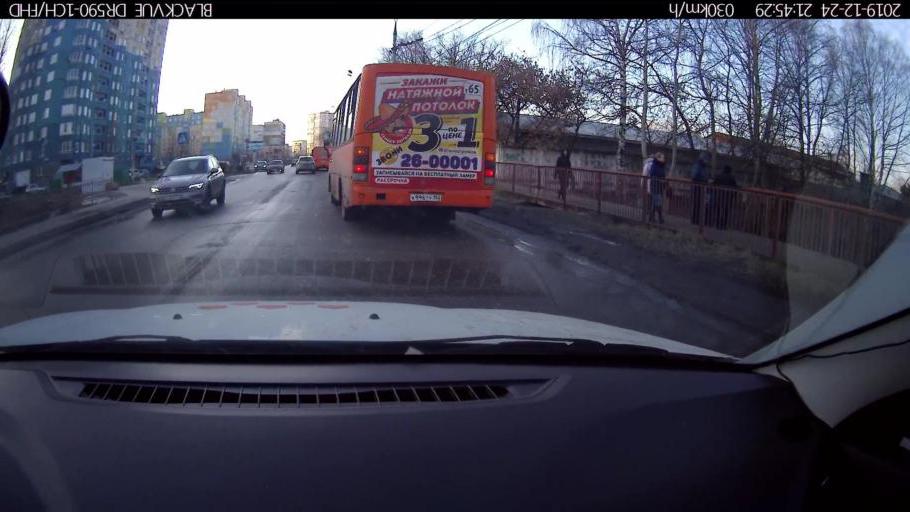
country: RU
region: Nizjnij Novgorod
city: Gorbatovka
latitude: 56.2401
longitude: 43.8424
